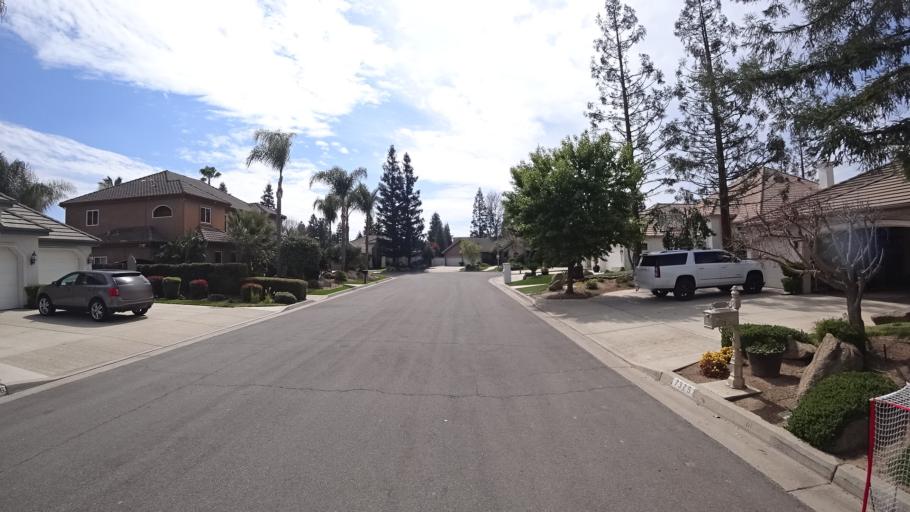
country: US
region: California
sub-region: Fresno County
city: West Park
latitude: 36.8427
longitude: -119.8833
